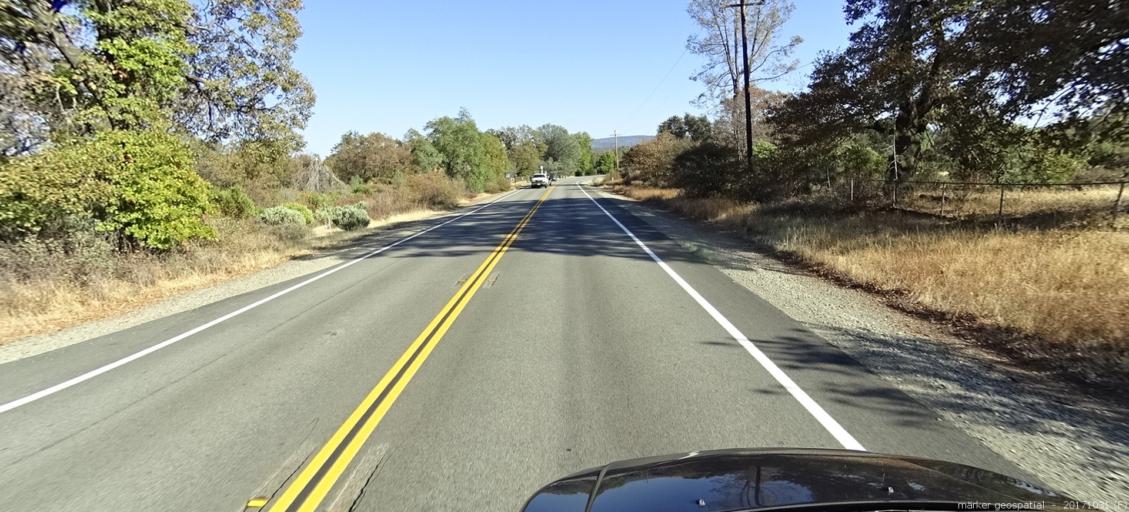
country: US
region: California
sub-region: Shasta County
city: Shingletown
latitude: 40.5135
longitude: -122.0235
